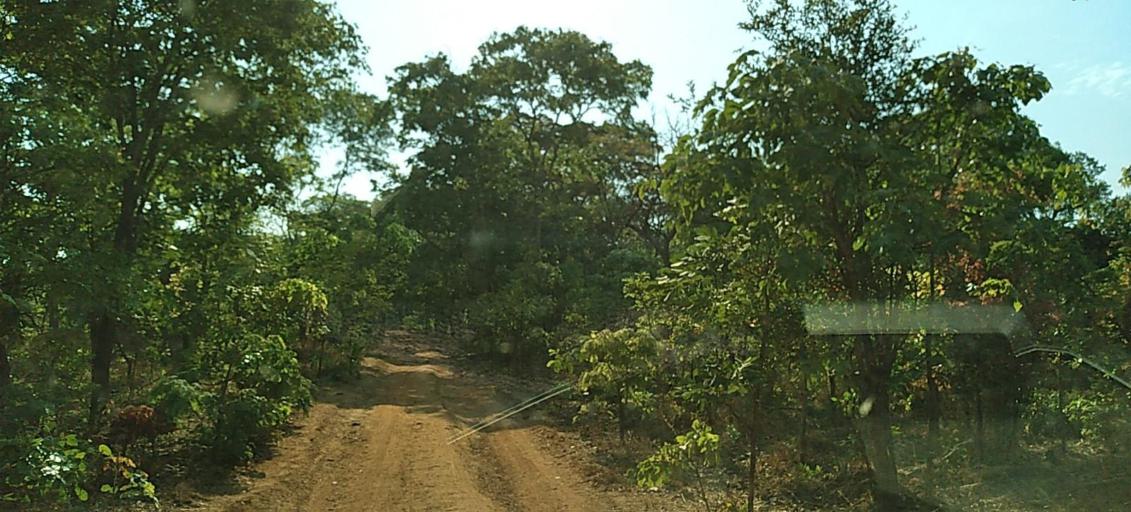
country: ZM
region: Copperbelt
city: Kalulushi
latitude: -13.0069
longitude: 27.7240
